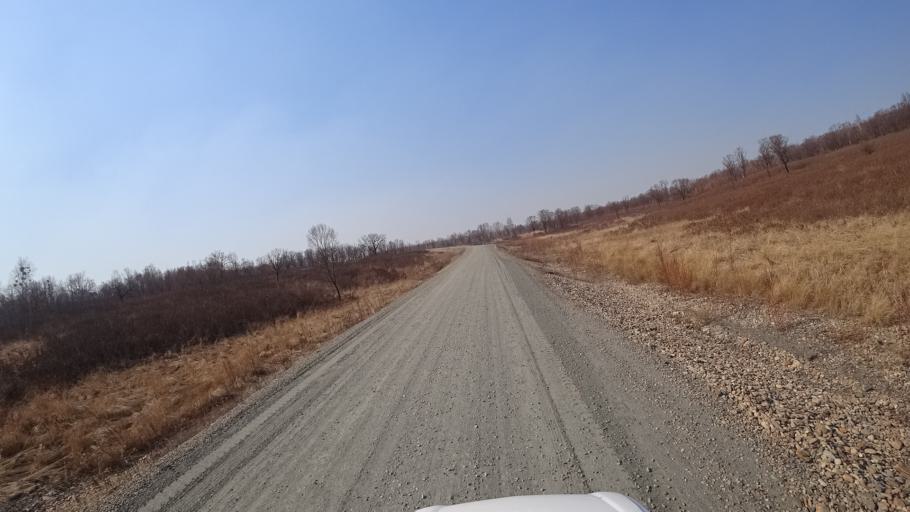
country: RU
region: Amur
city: Novobureyskiy
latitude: 49.8241
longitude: 129.9963
